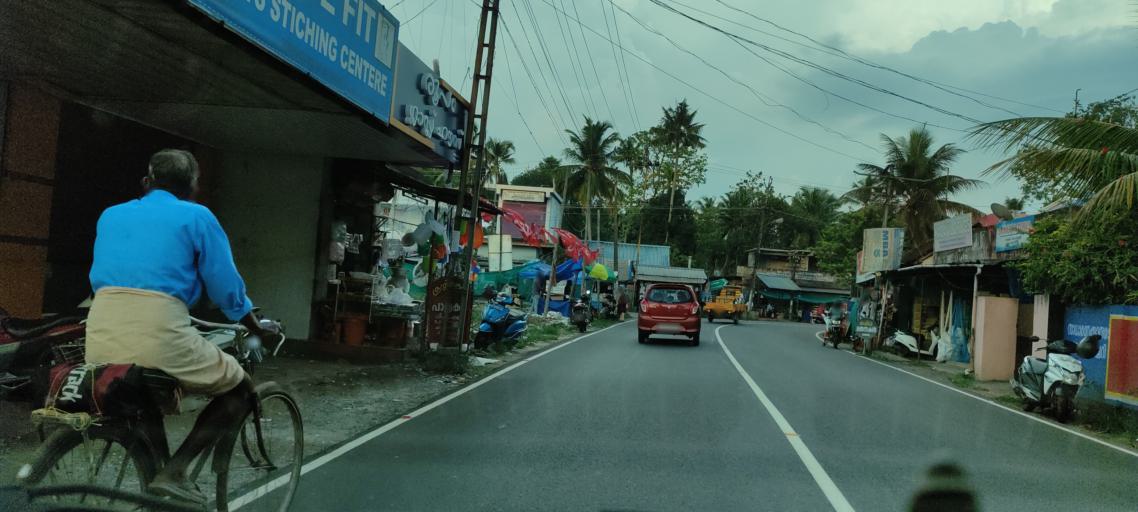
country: IN
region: Kerala
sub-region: Alappuzha
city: Arukutti
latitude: 9.8345
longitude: 76.3386
